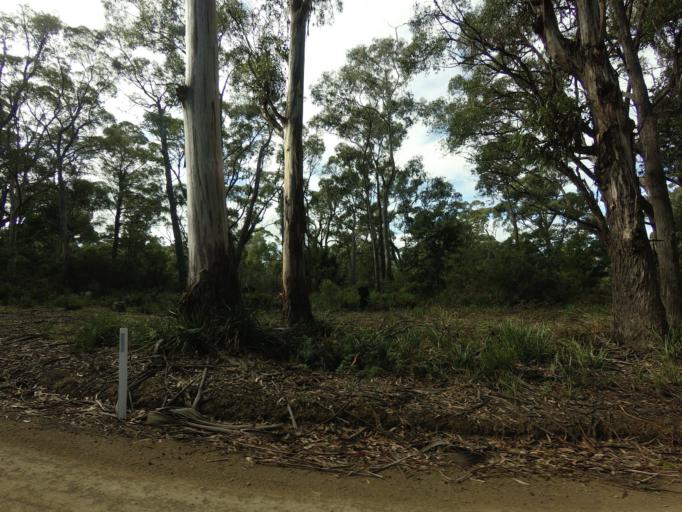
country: AU
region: Tasmania
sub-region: Clarence
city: Sandford
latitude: -43.0925
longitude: 147.7144
